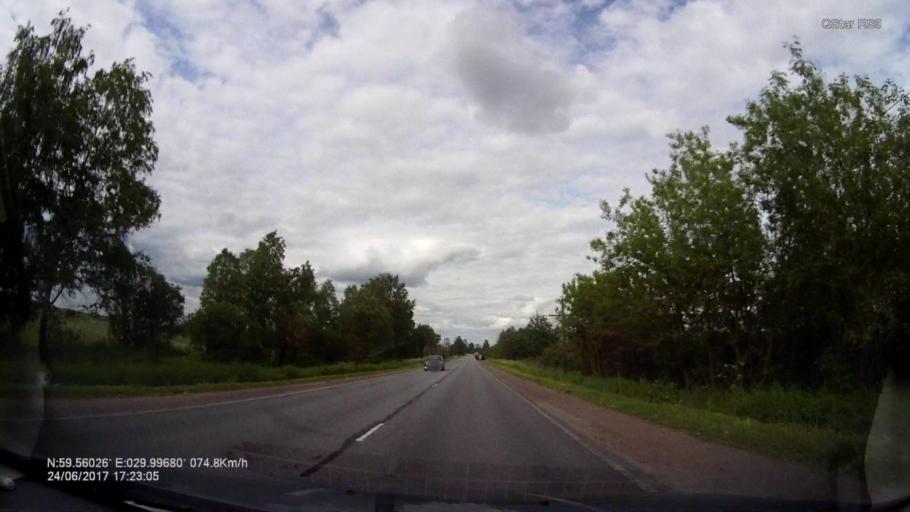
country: RU
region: Leningrad
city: Voyskovitsy
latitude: 59.5605
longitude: 29.9974
